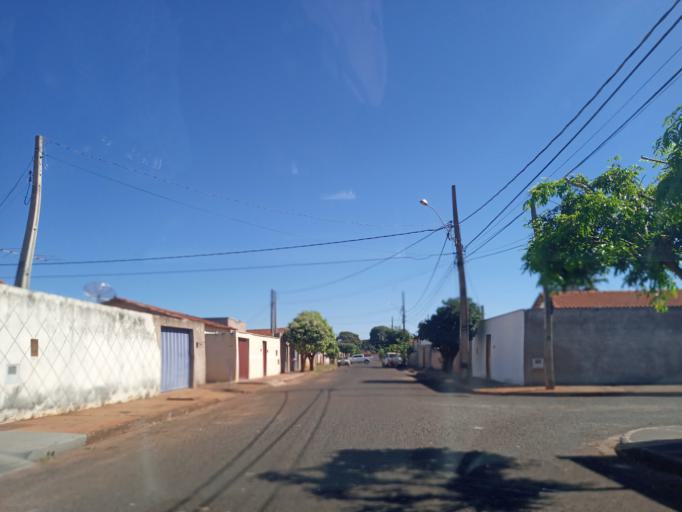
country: BR
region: Minas Gerais
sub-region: Ituiutaba
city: Ituiutaba
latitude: -18.9677
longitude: -49.4469
